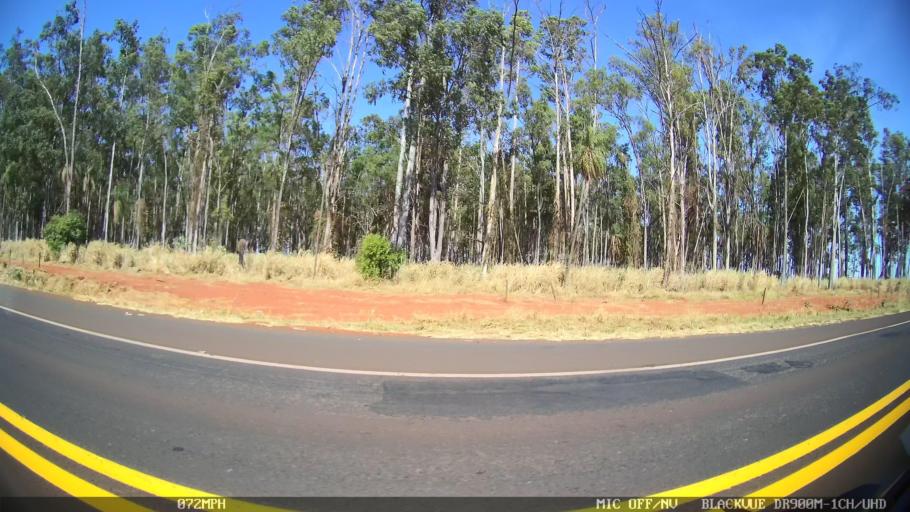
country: BR
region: Sao Paulo
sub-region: Barretos
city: Barretos
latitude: -20.4933
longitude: -48.5271
